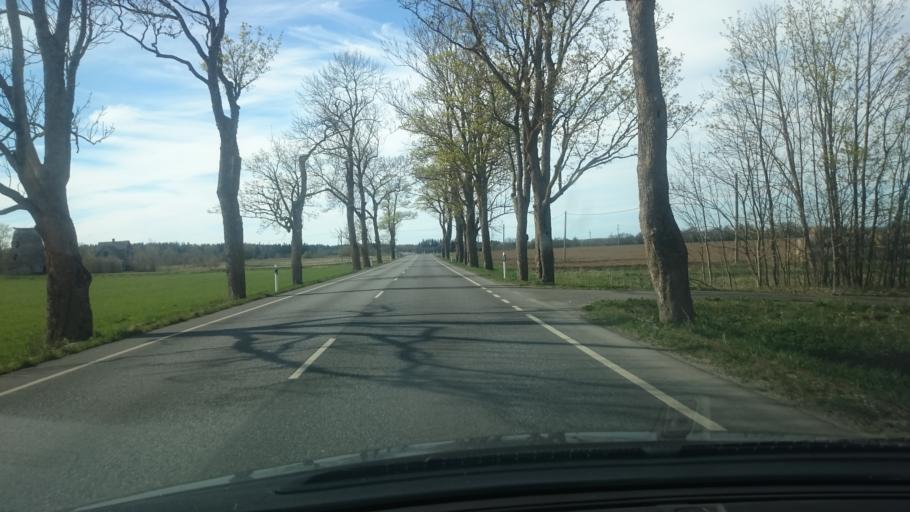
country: EE
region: Ida-Virumaa
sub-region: Johvi vald
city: Johvi
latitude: 59.2748
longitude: 27.5098
